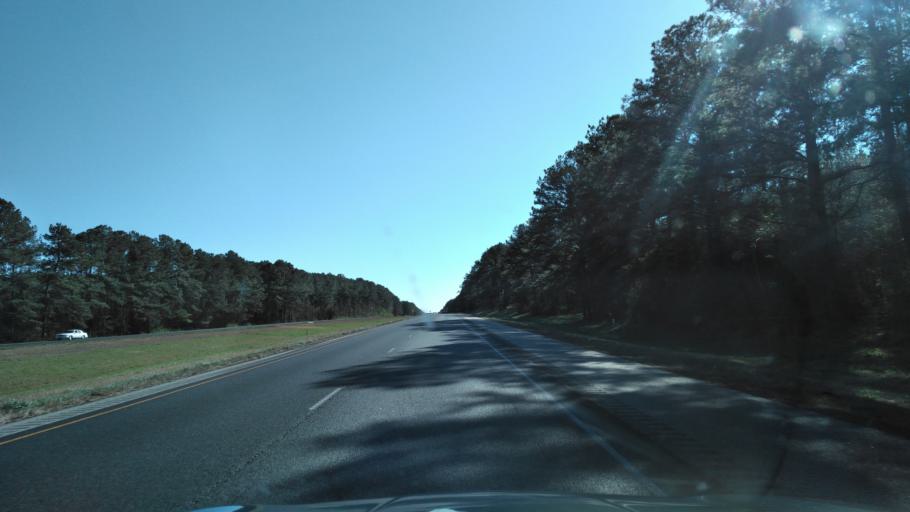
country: US
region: Alabama
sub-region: Butler County
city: Georgiana
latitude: 31.6916
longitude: -86.7474
